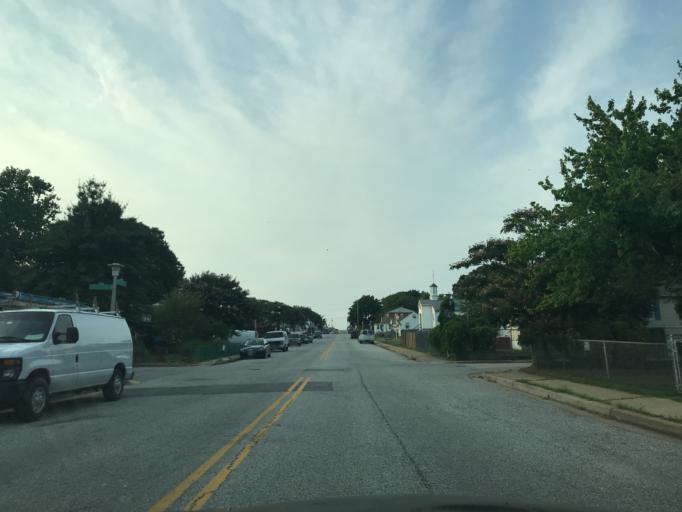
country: US
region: Maryland
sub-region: Baltimore County
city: Dundalk
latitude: 39.2727
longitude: -76.5403
